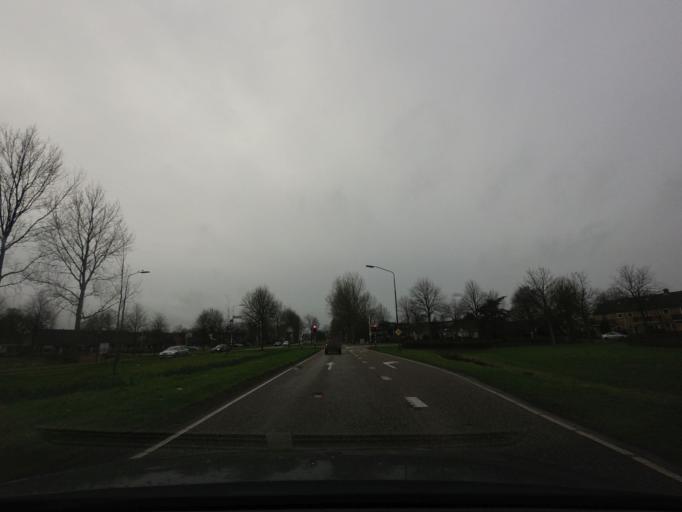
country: NL
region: North Holland
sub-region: Gemeente Schagen
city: Schagen
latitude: 52.7822
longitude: 4.8003
